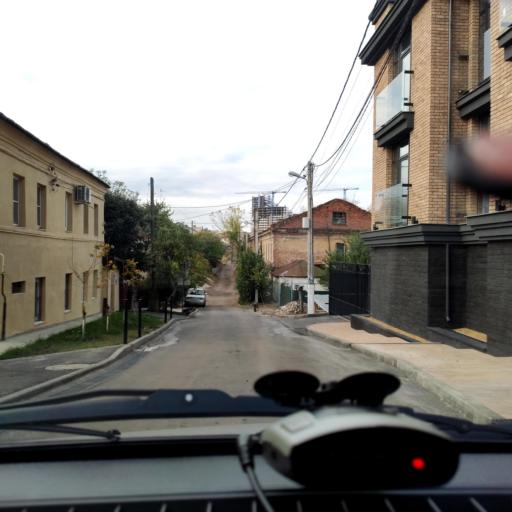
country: RU
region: Voronezj
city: Voronezh
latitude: 51.6556
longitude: 39.2040
